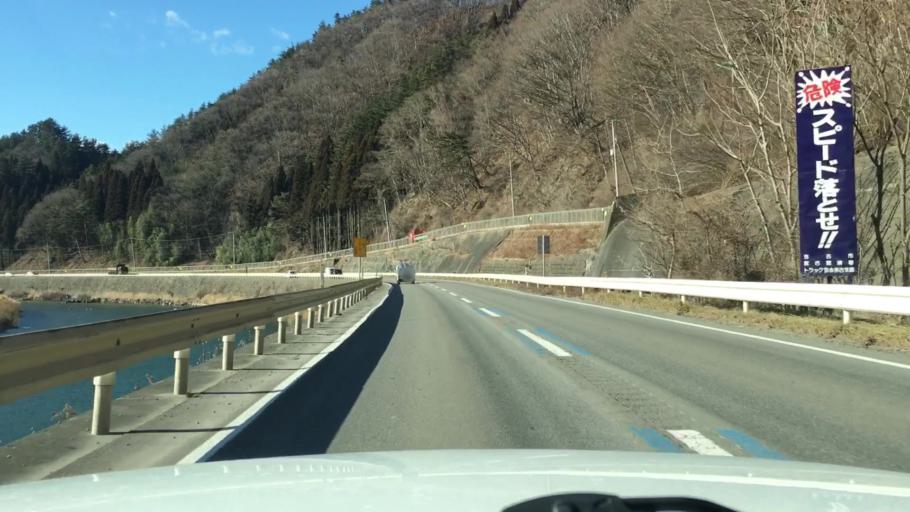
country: JP
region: Iwate
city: Miyako
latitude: 39.6354
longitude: 141.8474
